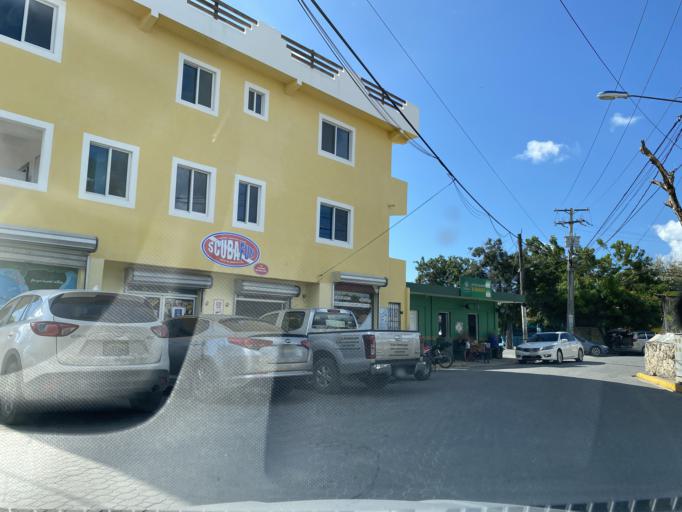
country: DO
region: La Romana
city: La Romana
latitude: 18.3684
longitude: -68.8393
